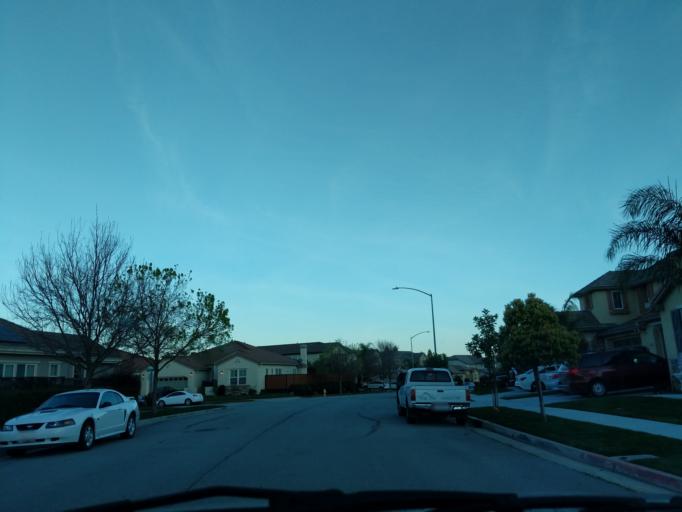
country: US
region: California
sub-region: Santa Clara County
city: Gilroy
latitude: 37.0347
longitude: -121.6085
